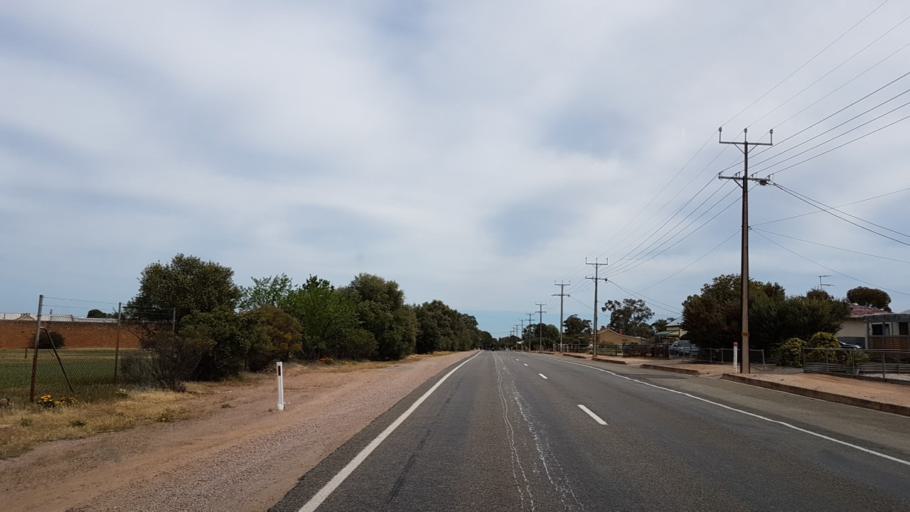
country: AU
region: South Australia
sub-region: Port Pirie City and Dists
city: Crystal Brook
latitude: -33.2594
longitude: 138.3566
